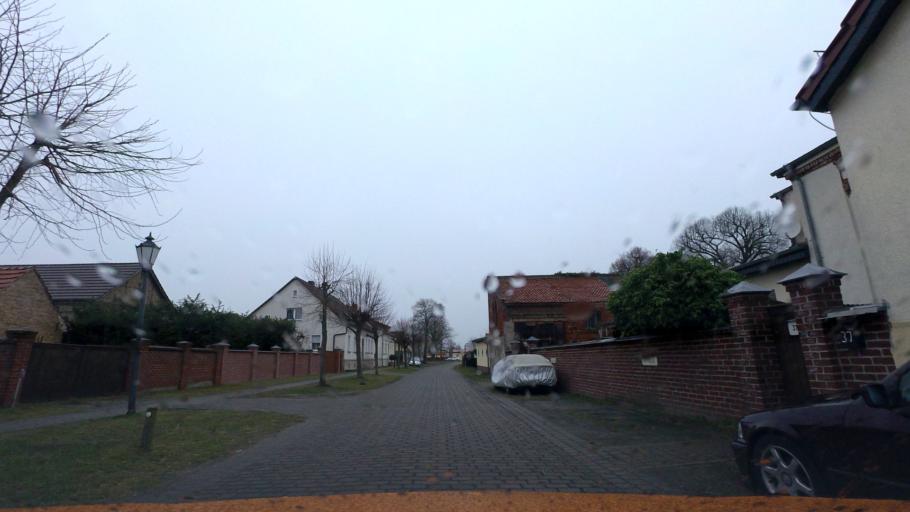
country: DE
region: Brandenburg
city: Brieselang
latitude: 52.6545
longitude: 12.9787
